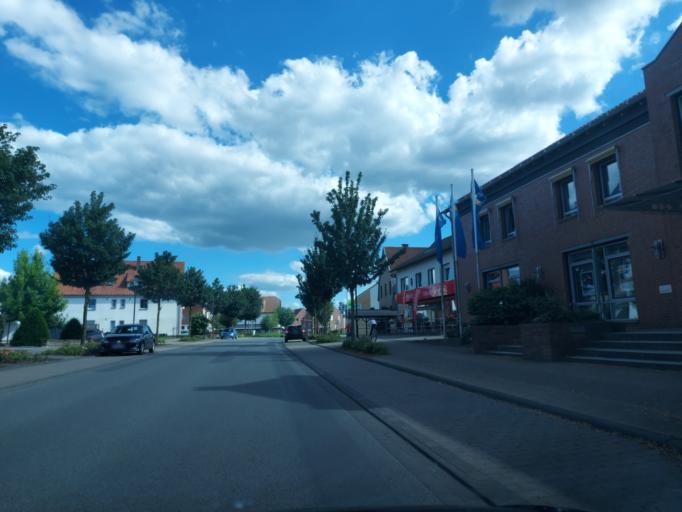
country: DE
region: Lower Saxony
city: Hilter
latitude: 52.1368
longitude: 8.1479
